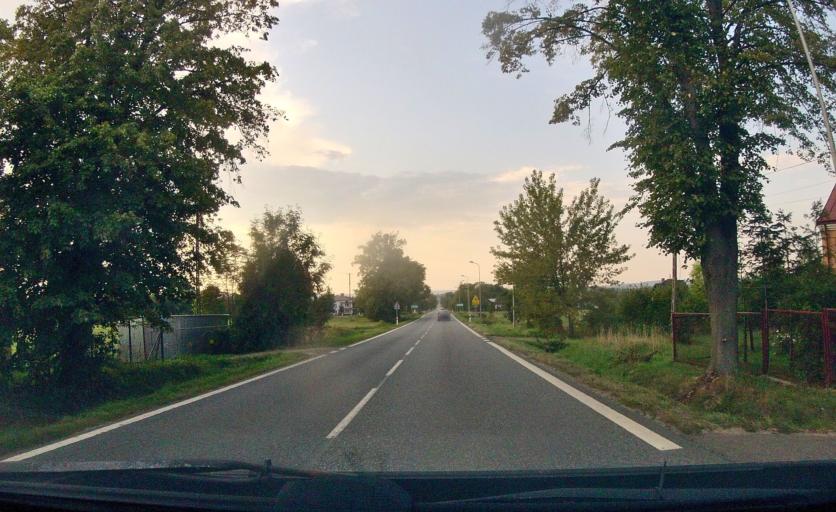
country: PL
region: Subcarpathian Voivodeship
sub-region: Powiat jasielski
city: Nowy Zmigrod
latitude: 49.5888
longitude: 21.5433
